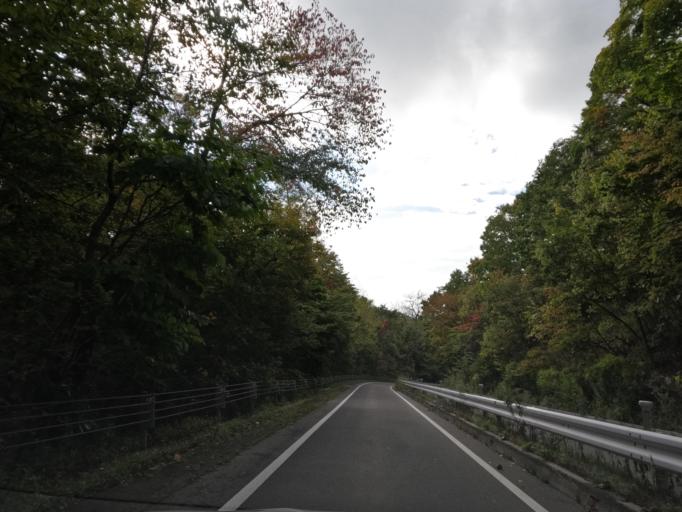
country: JP
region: Hokkaido
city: Chitose
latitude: 42.8038
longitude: 141.5832
